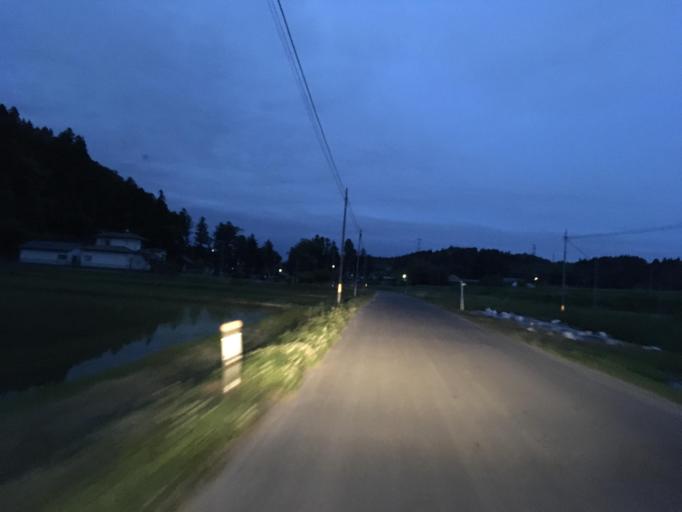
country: JP
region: Miyagi
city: Furukawa
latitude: 38.7858
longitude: 140.9537
